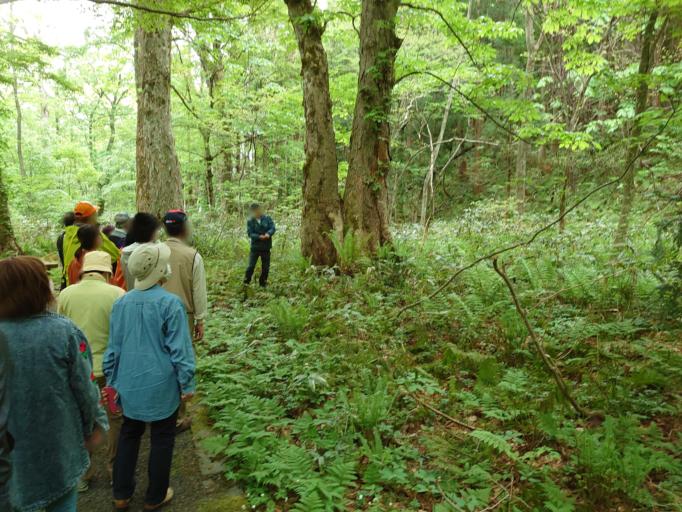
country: JP
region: Iwate
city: Ichinoseki
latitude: 39.0041
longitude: 140.8524
